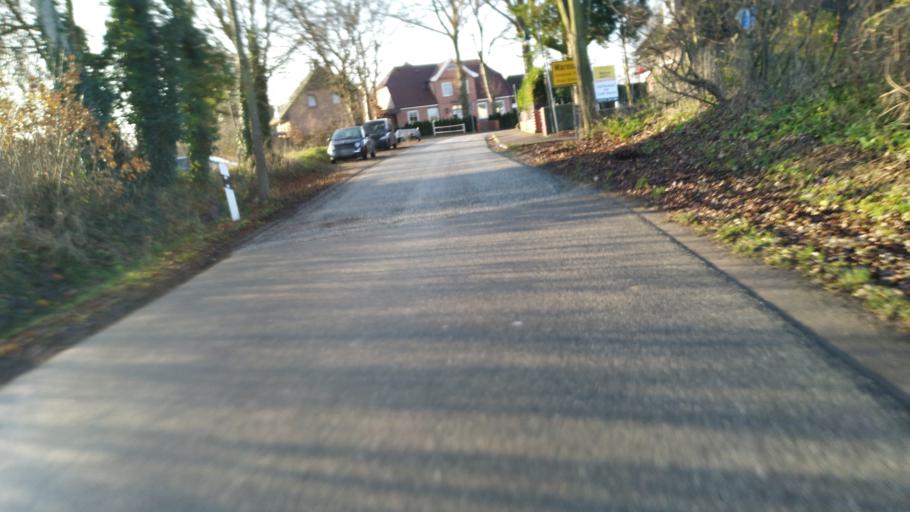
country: DE
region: Schleswig-Holstein
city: Travemuende
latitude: 53.9678
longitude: 10.8235
